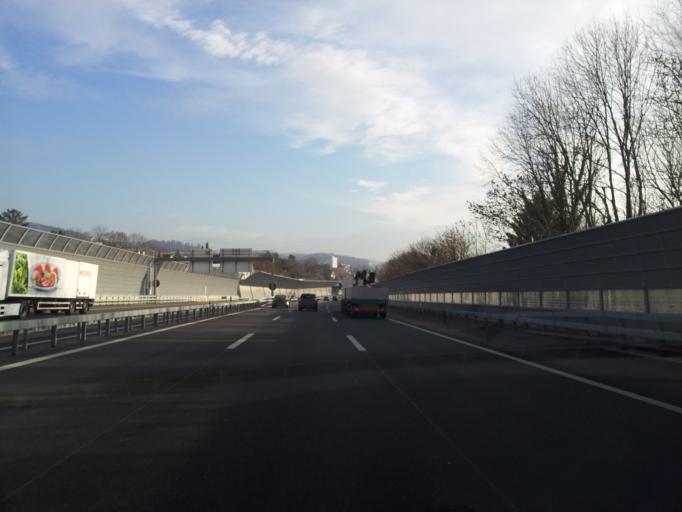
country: CH
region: Zurich
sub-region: Bezirk Dietikon
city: Unterengstringen
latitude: 47.4104
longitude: 8.4433
